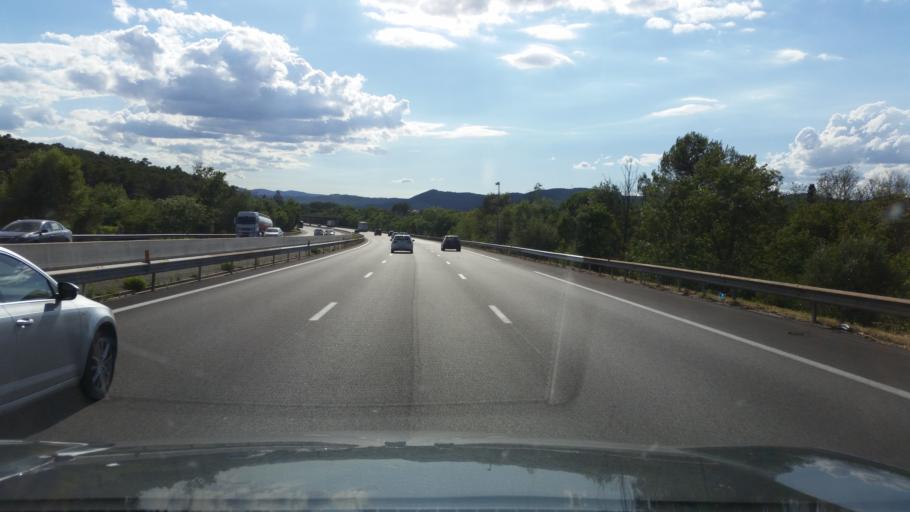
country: FR
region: Provence-Alpes-Cote d'Azur
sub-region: Departement du Var
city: Les Arcs
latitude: 43.4520
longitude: 6.5120
